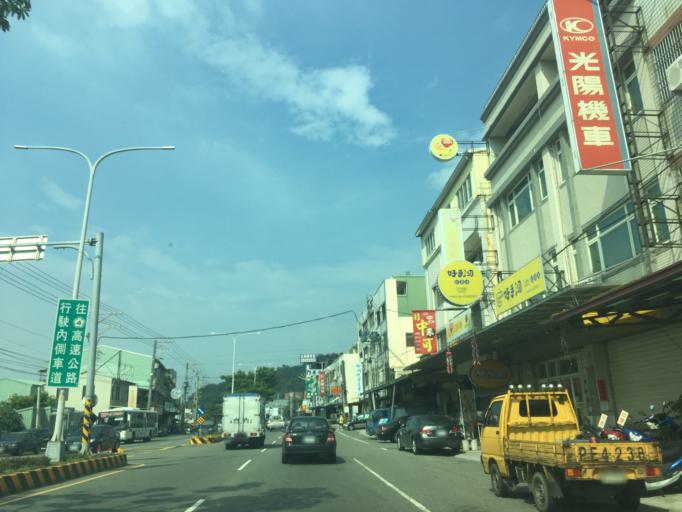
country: TW
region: Taiwan
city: Fengyuan
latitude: 24.2649
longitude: 120.7451
